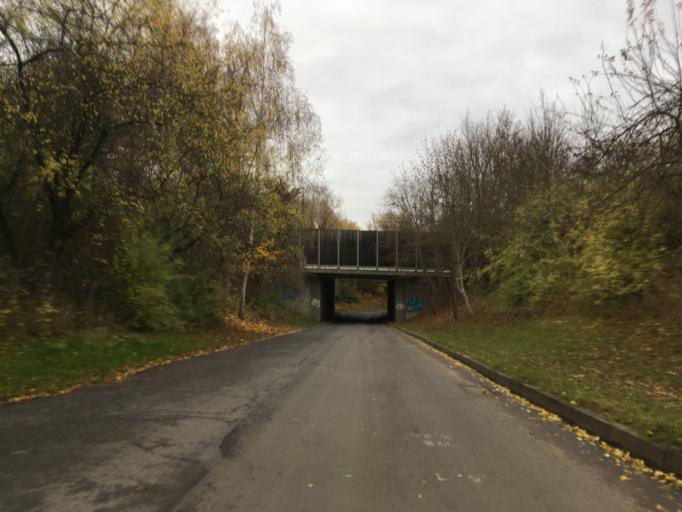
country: DE
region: Brandenburg
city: Frankfurt (Oder)
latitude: 52.3137
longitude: 14.5476
